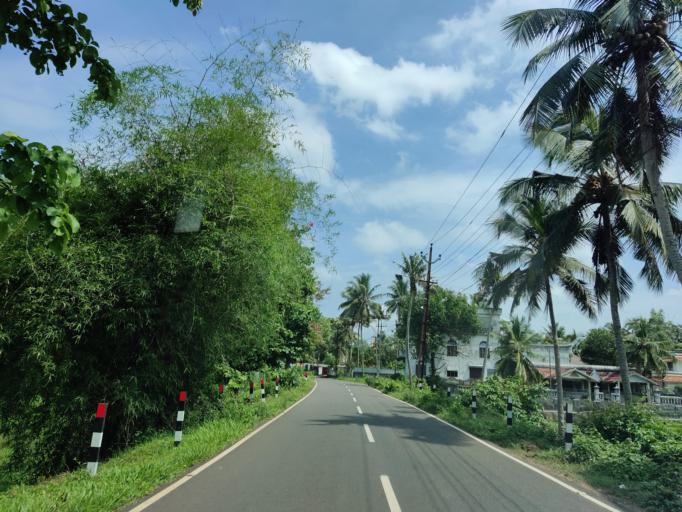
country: IN
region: Kerala
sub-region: Alappuzha
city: Mavelikara
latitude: 9.2804
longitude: 76.5678
